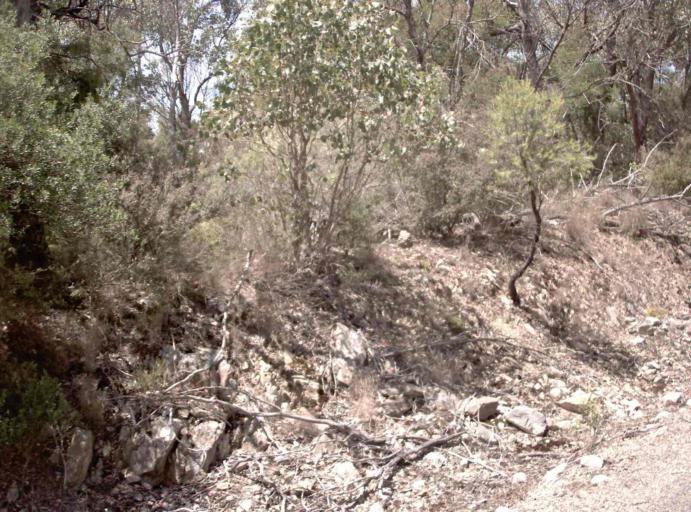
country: AU
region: Victoria
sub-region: East Gippsland
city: Lakes Entrance
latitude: -37.5709
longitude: 147.8910
